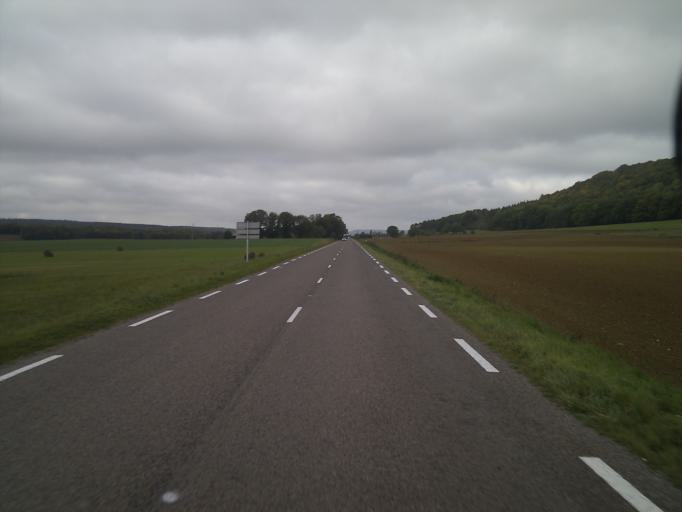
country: FR
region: Champagne-Ardenne
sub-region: Departement de la Haute-Marne
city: Doulaincourt-Saucourt
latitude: 48.2615
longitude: 5.3817
